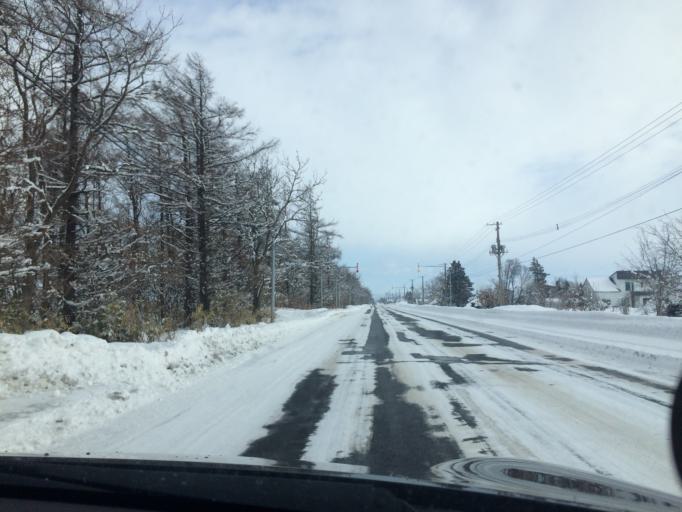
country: JP
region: Hokkaido
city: Kitahiroshima
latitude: 43.0400
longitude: 141.6194
